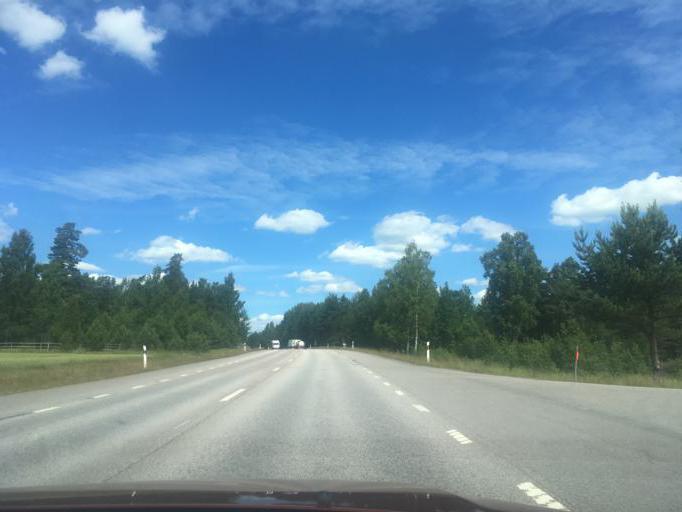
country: SE
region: OEstergoetland
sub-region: Soderkopings Kommun
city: Soederkoeping
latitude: 58.4568
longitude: 16.3658
